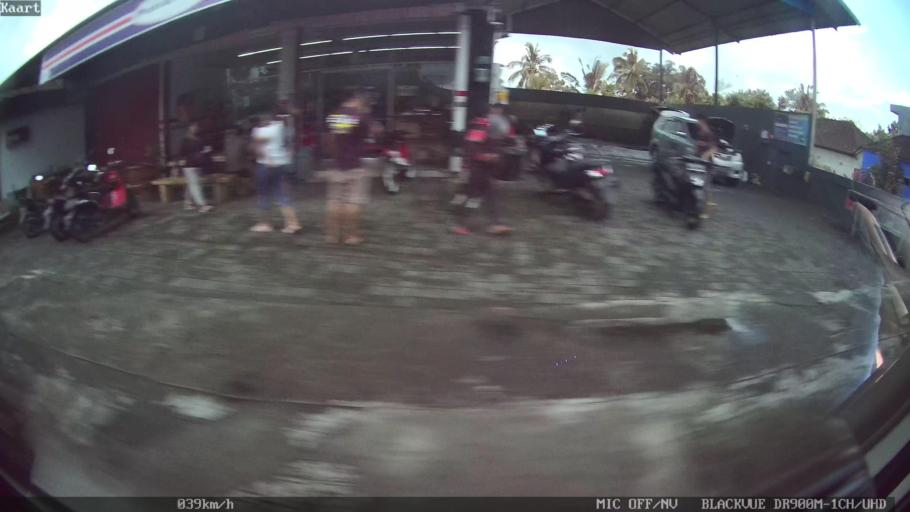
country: ID
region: Bali
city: Pohgending Kawan
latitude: -8.4351
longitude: 115.1429
